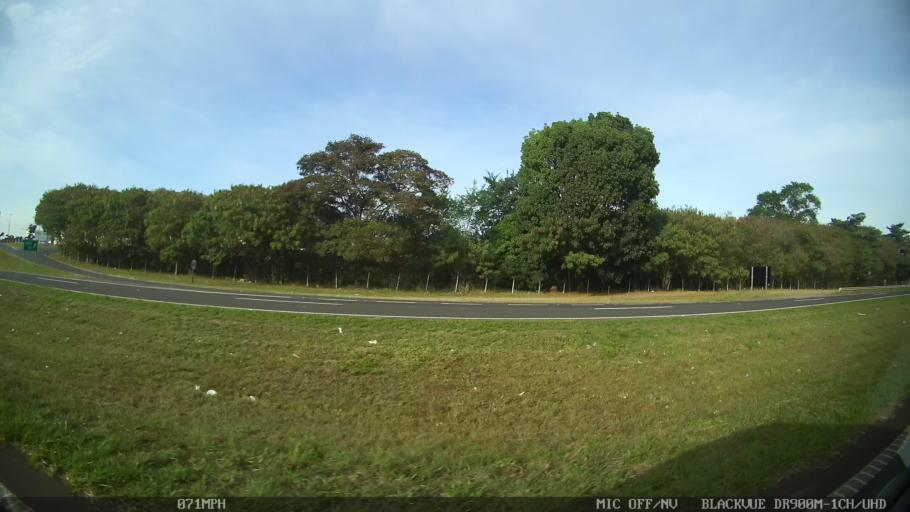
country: BR
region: Sao Paulo
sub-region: Piracicaba
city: Piracicaba
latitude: -22.7223
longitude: -47.5980
